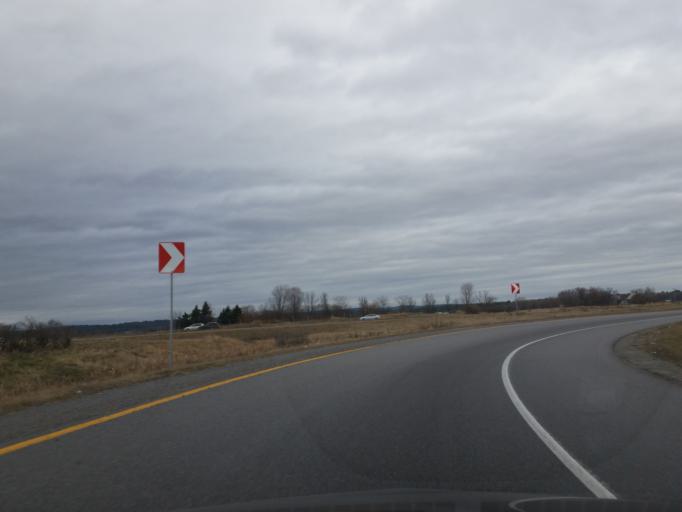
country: CA
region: Quebec
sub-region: Outaouais
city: Gatineau
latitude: 45.5058
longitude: -75.6808
